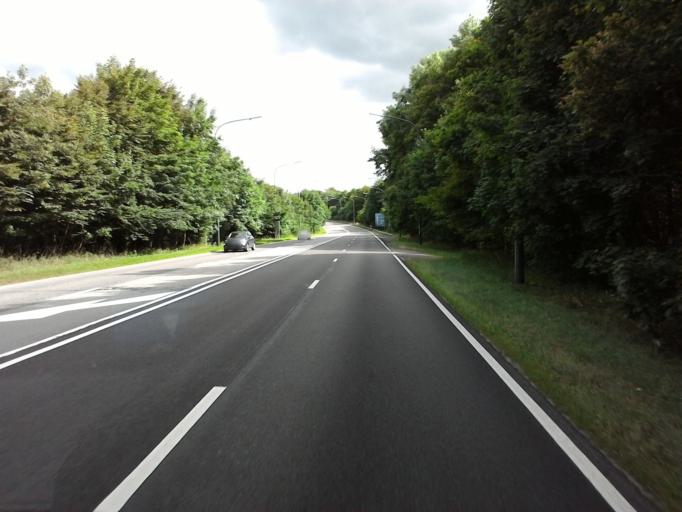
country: BE
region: Wallonia
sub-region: Province du Luxembourg
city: Martelange
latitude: 49.7927
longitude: 5.7420
